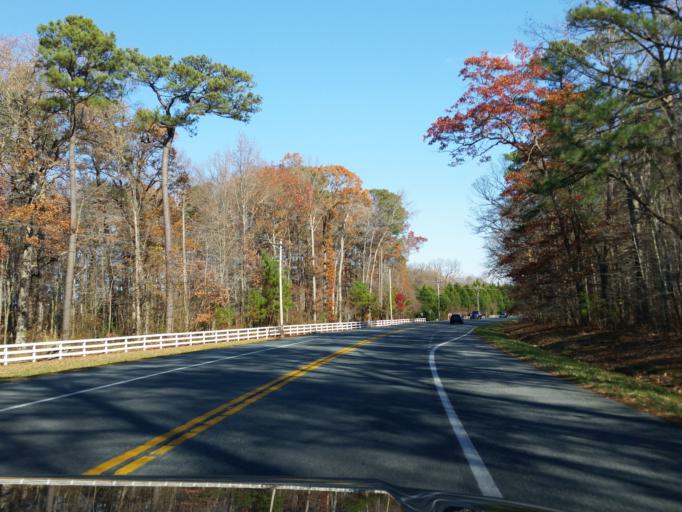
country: US
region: Maryland
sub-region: Talbot County
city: Easton
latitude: 38.7768
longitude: -76.1360
